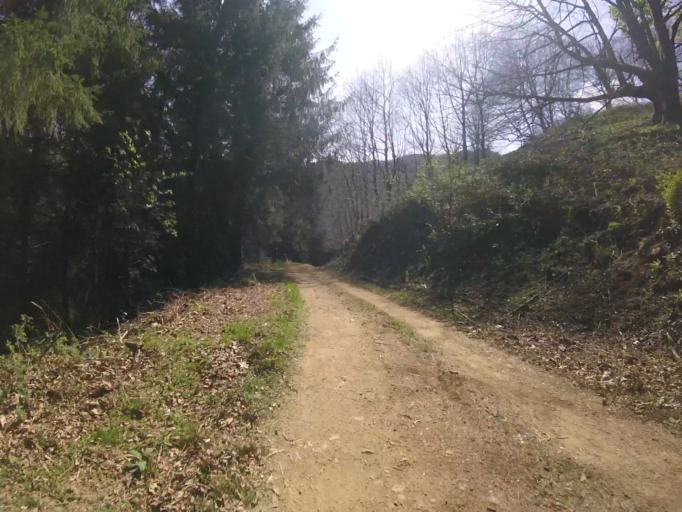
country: ES
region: Basque Country
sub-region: Provincia de Guipuzcoa
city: Irun
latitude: 43.2532
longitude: -1.8107
